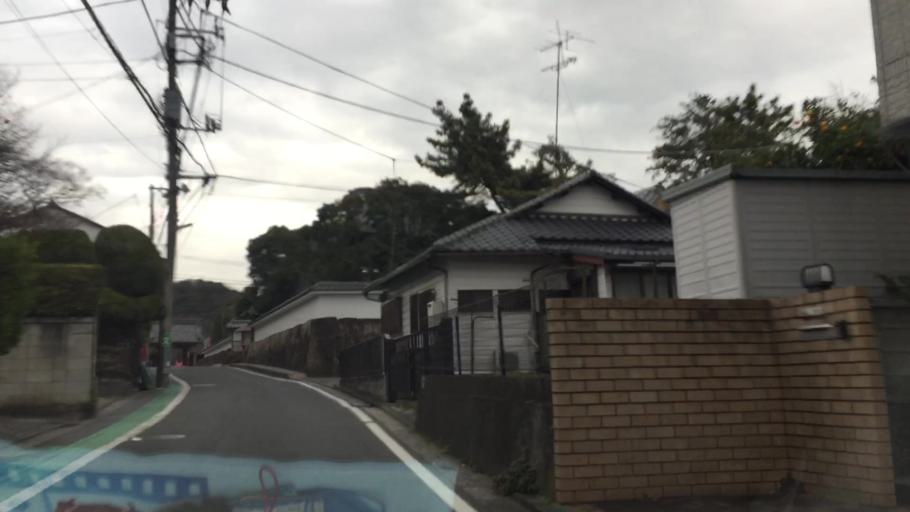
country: JP
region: Kanagawa
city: Yokosuka
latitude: 35.3410
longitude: 139.6291
